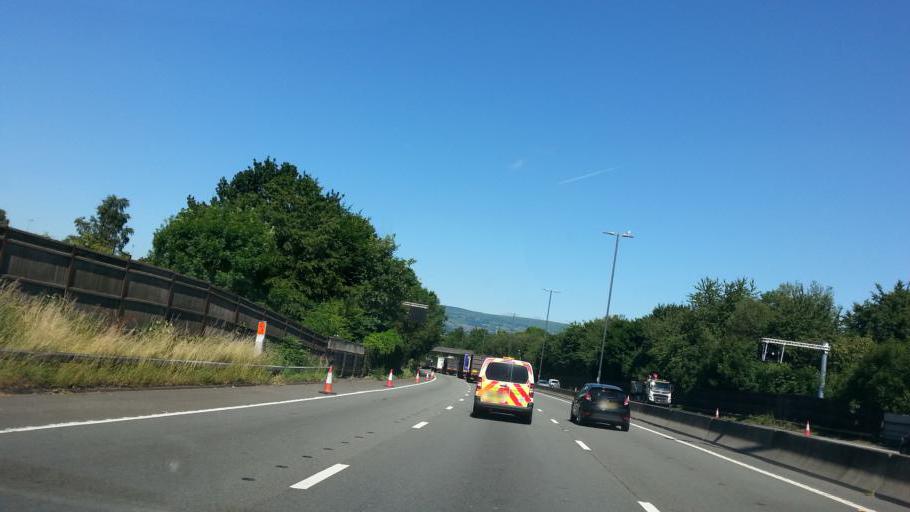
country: GB
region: Wales
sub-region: Newport
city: Caerleon
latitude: 51.5989
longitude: -2.9674
